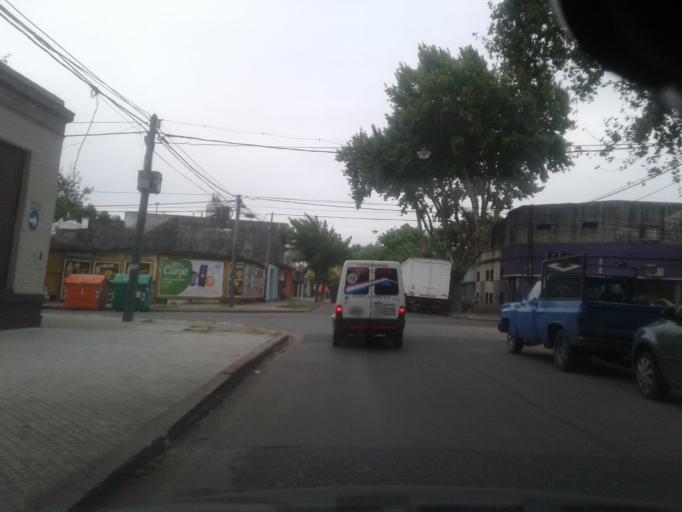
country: AR
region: Santa Fe
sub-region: Departamento de Rosario
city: Rosario
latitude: -32.9487
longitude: -60.6773
